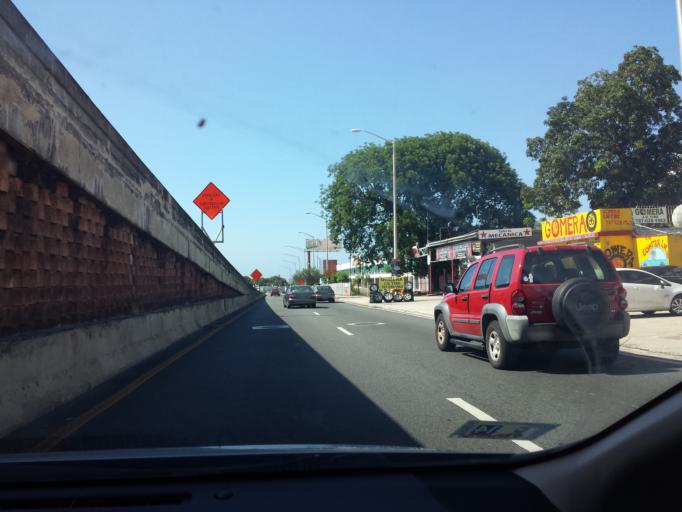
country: PR
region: Trujillo Alto
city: Trujillo Alto
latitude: 18.3990
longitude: -66.0313
